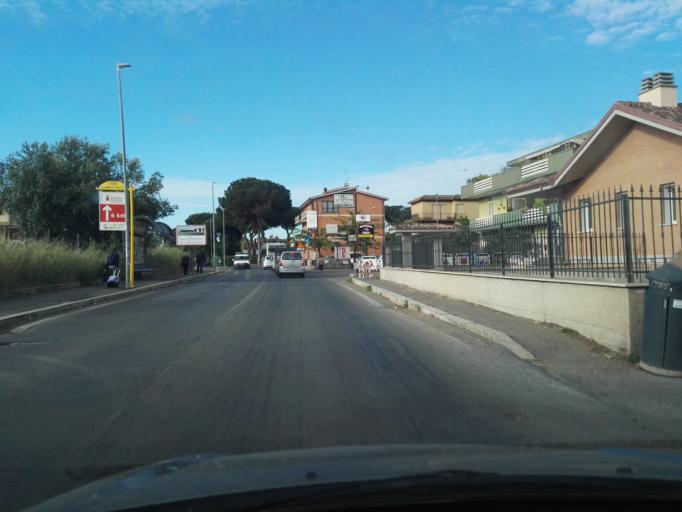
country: IT
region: Latium
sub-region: Citta metropolitana di Roma Capitale
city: Selcetta
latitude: 41.7675
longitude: 12.4779
